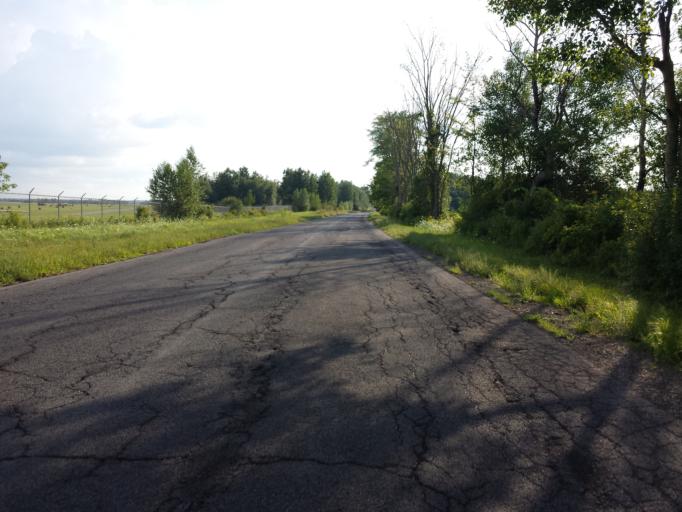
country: US
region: New York
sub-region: St. Lawrence County
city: Potsdam
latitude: 44.6823
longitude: -74.9436
